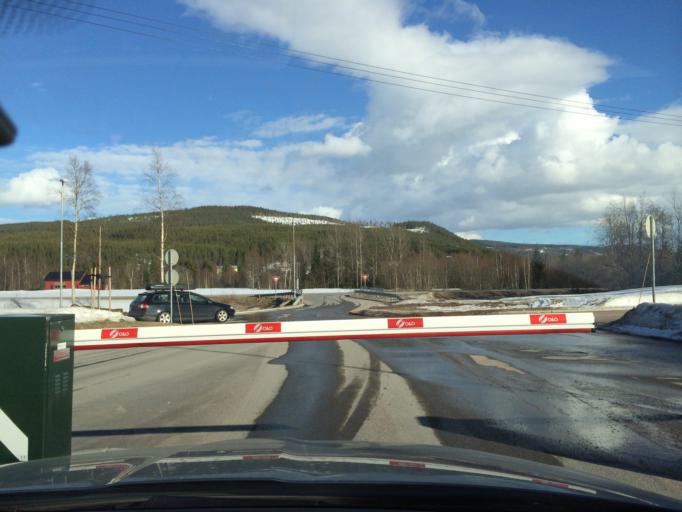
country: NO
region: Hedmark
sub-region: Trysil
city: Innbygda
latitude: 61.3417
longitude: 12.2189
